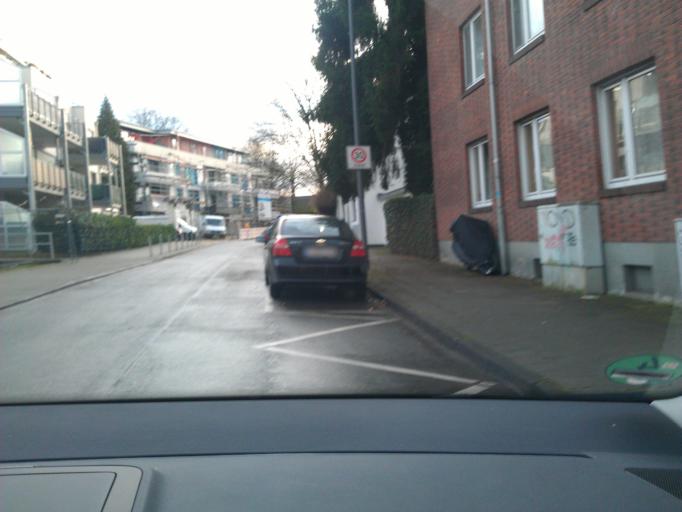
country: DE
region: North Rhine-Westphalia
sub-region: Regierungsbezirk Koln
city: Aachen
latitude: 50.7613
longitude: 6.0868
